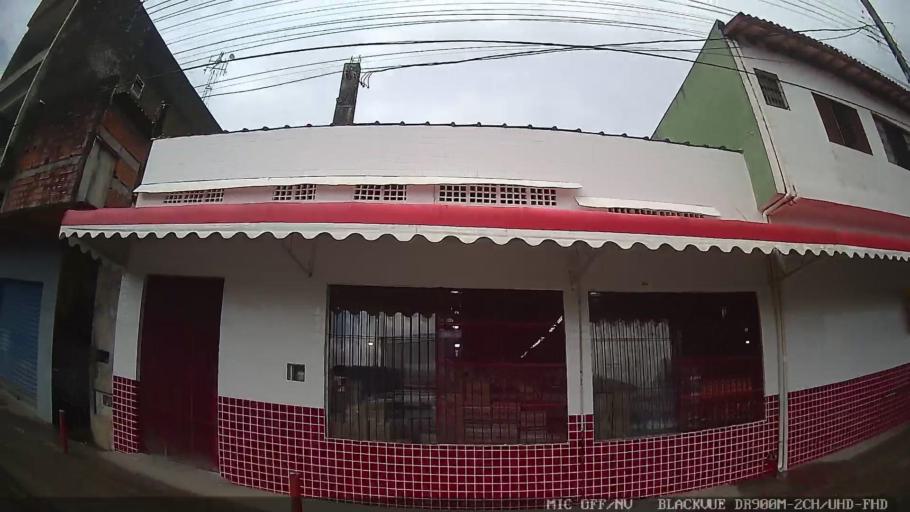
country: BR
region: Sao Paulo
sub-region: Itanhaem
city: Itanhaem
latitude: -24.1634
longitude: -46.7918
